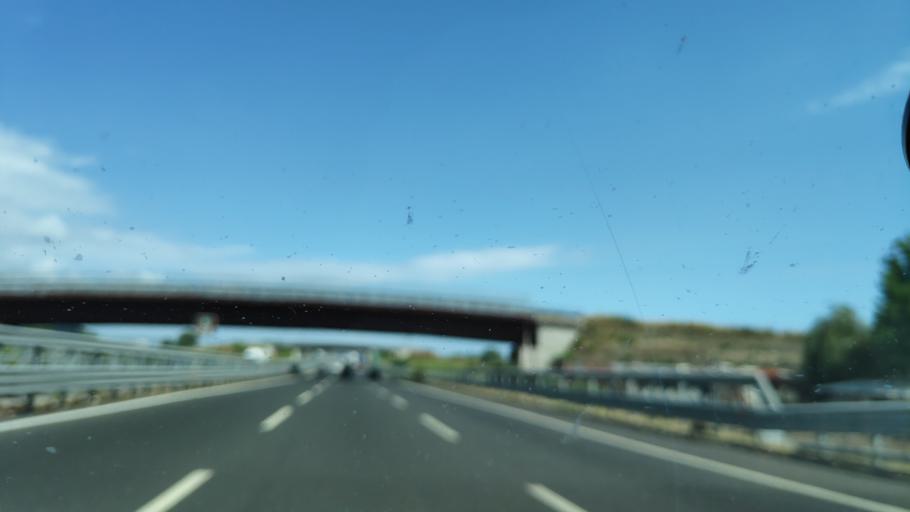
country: IT
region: Campania
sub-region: Provincia di Salerno
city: Pontecagnano
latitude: 40.6517
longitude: 14.8755
